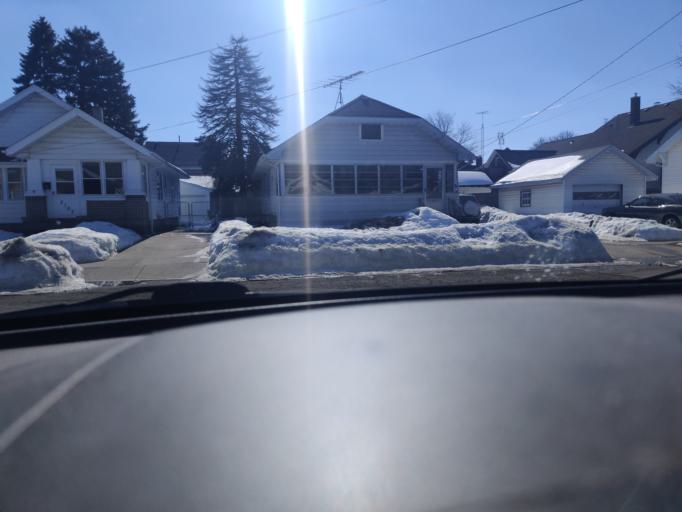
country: US
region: Wisconsin
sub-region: Kenosha County
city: Kenosha
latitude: 42.5683
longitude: -87.8346
